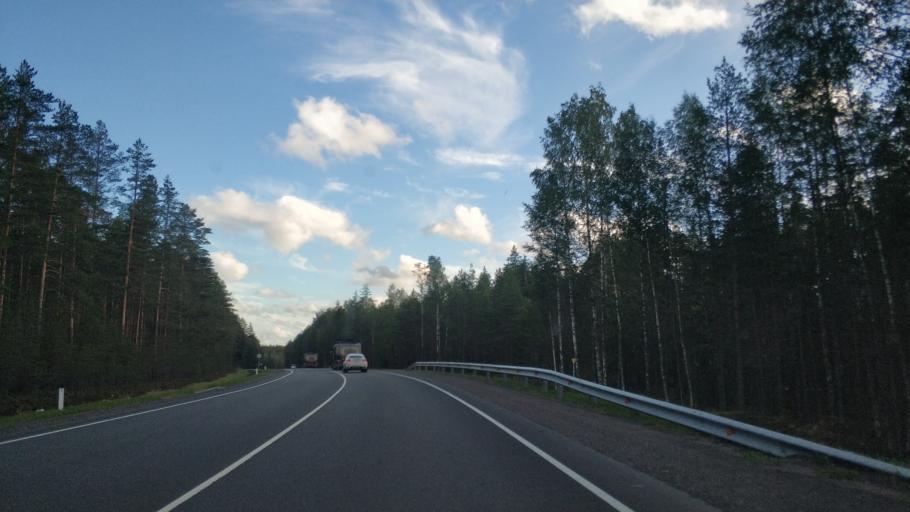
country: RU
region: Leningrad
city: Priozersk
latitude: 60.8814
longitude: 30.1606
